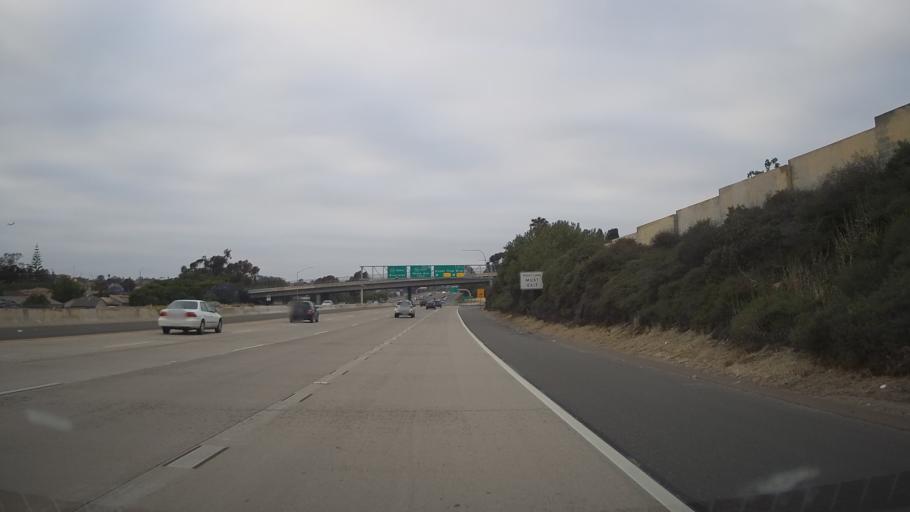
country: US
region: California
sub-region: San Diego County
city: National City
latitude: 32.6986
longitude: -117.1207
